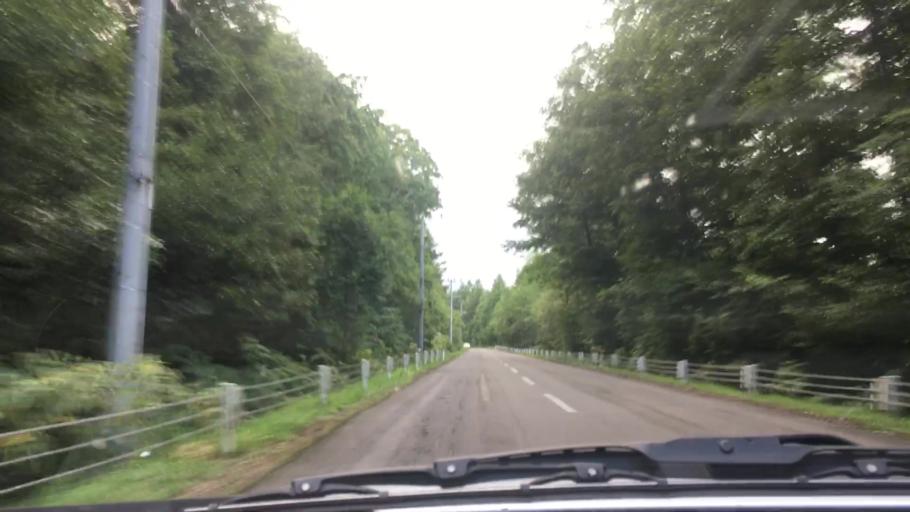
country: JP
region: Hokkaido
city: Otofuke
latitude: 43.1460
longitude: 142.8744
